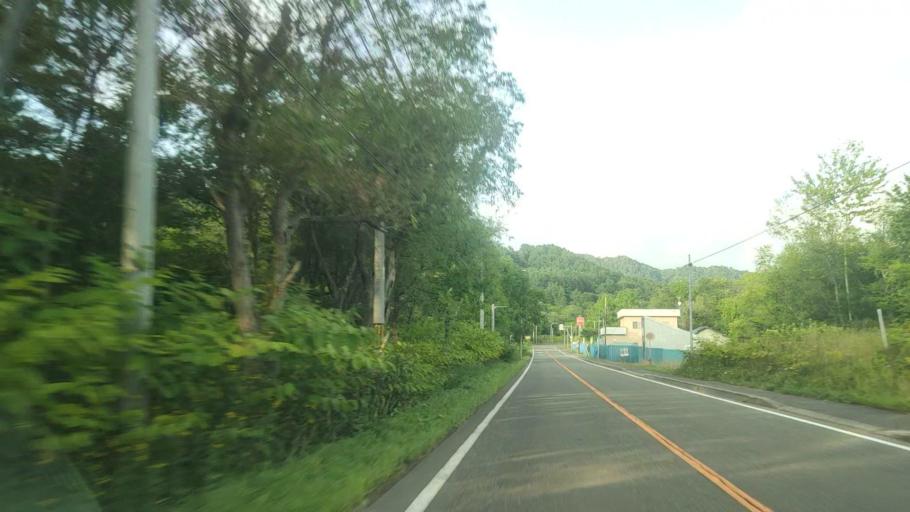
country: JP
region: Hokkaido
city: Iwamizawa
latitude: 43.0213
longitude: 142.0725
